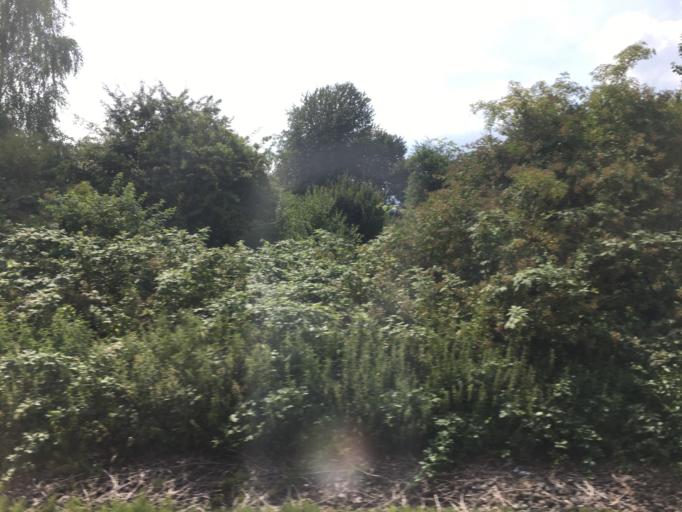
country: DE
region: Hesse
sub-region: Regierungsbezirk Darmstadt
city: Steinbach am Taunus
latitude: 50.1766
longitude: 8.5863
